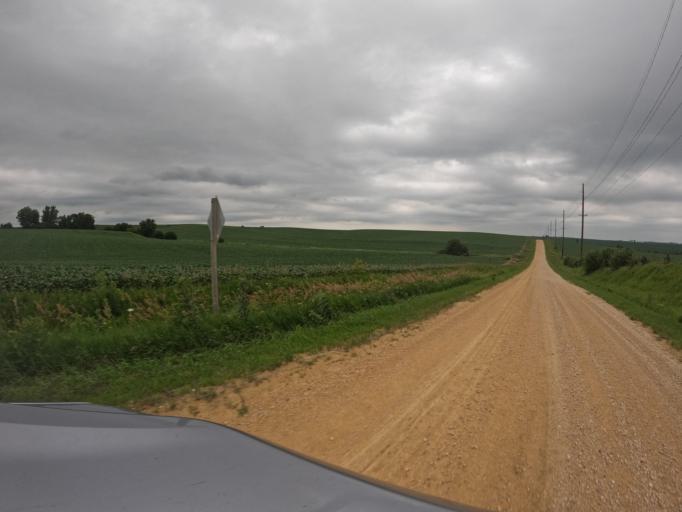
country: US
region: Iowa
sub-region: Clinton County
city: De Witt
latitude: 41.9382
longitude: -90.6038
